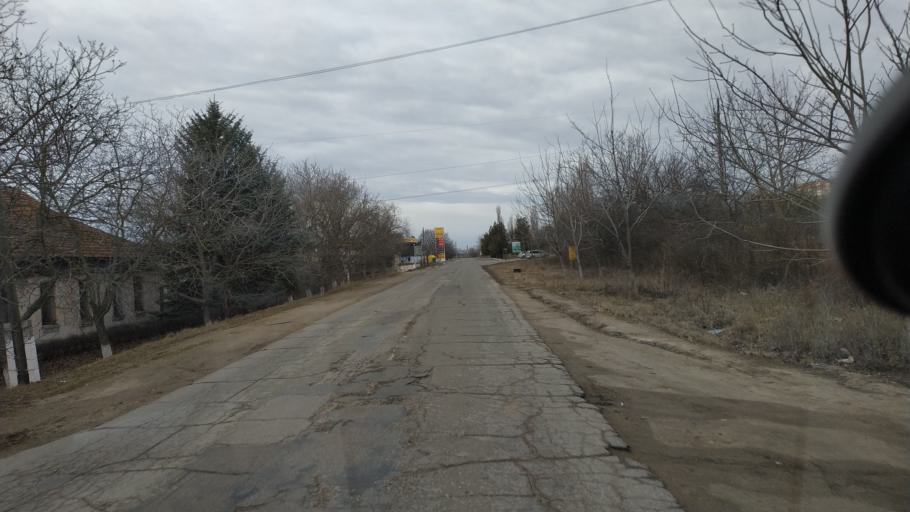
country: MD
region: Criuleni
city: Criuleni
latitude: 47.2222
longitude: 29.1509
